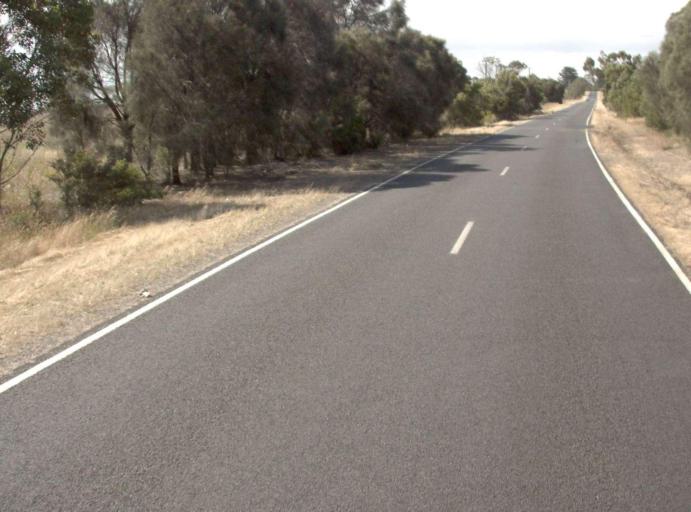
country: AU
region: Victoria
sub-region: Wellington
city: Sale
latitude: -38.3363
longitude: 147.1631
